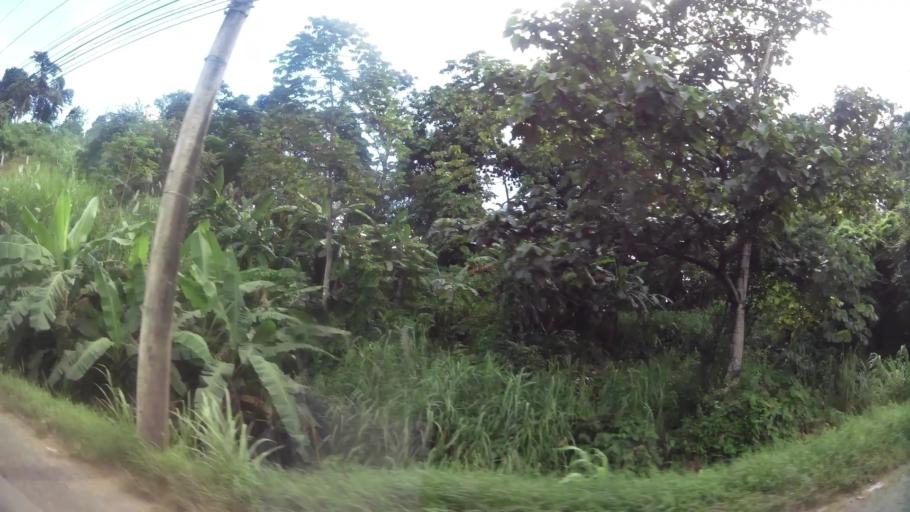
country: PA
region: Panama
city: Panama
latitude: 9.0344
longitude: -79.5401
